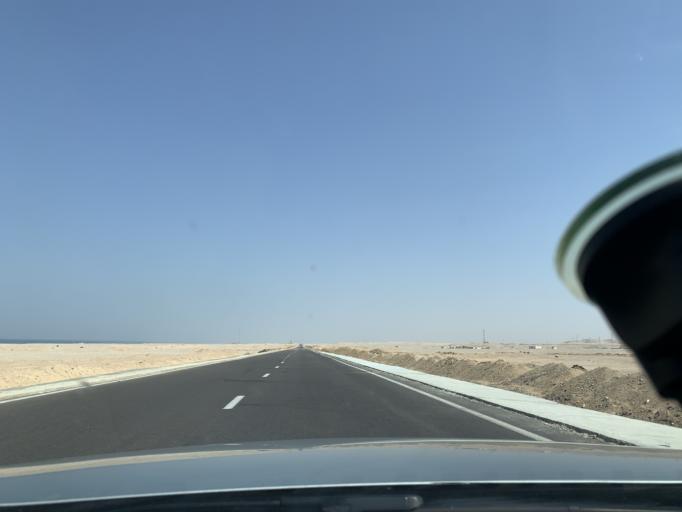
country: EG
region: As Suways
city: Ain Sukhna
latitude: 28.8751
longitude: 32.6629
